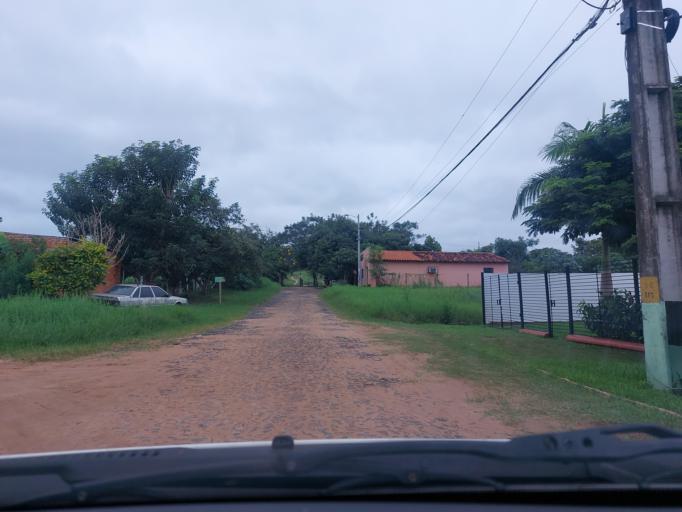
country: PY
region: San Pedro
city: Guayaybi
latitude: -24.6679
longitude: -56.4343
